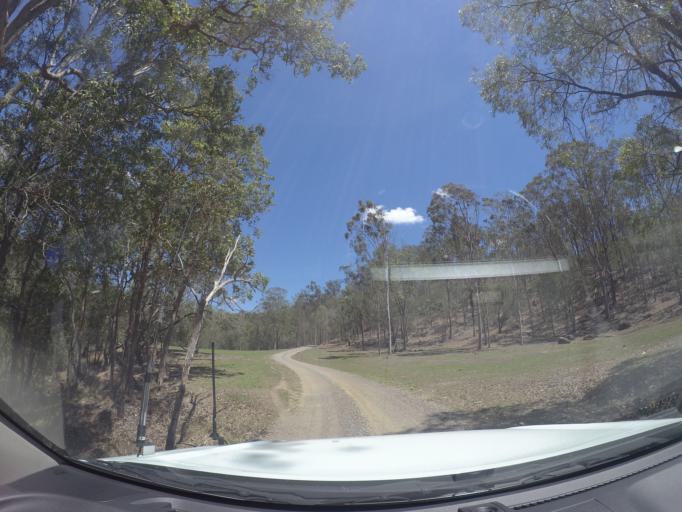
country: AU
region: Queensland
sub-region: Ipswich
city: Deebing Heights
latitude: -27.7605
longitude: 152.8097
